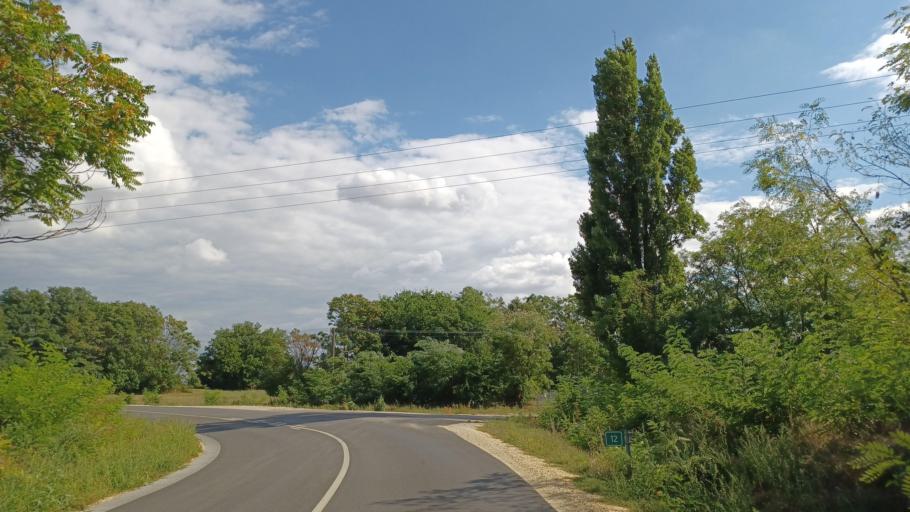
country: HU
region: Tolna
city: Nagydorog
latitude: 46.6001
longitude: 18.7020
